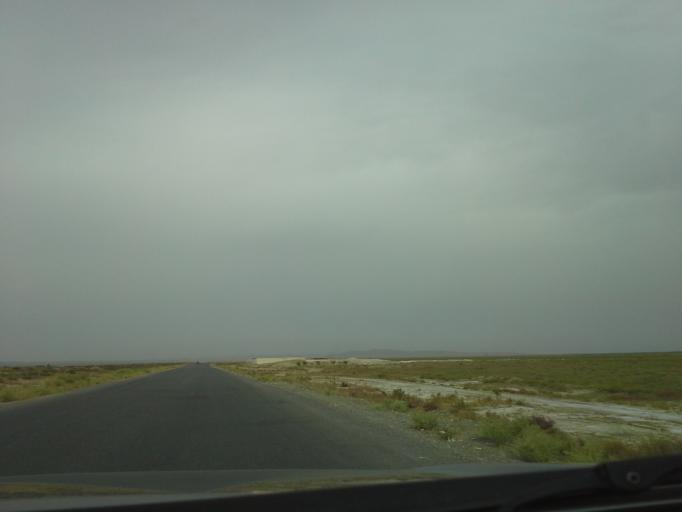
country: TM
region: Lebap
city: Atamyrat
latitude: 37.7314
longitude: 65.5030
